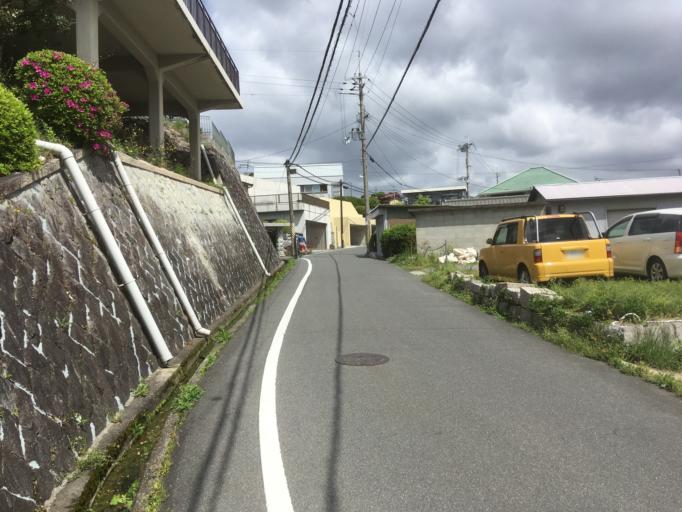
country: JP
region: Nara
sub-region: Ikoma-shi
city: Ikoma
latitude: 34.6971
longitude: 135.6929
